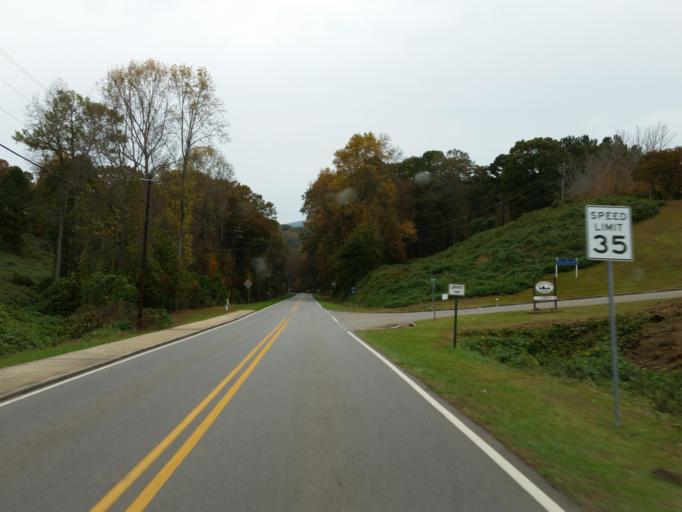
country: US
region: Georgia
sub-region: Pickens County
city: Jasper
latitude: 34.4734
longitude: -84.4225
